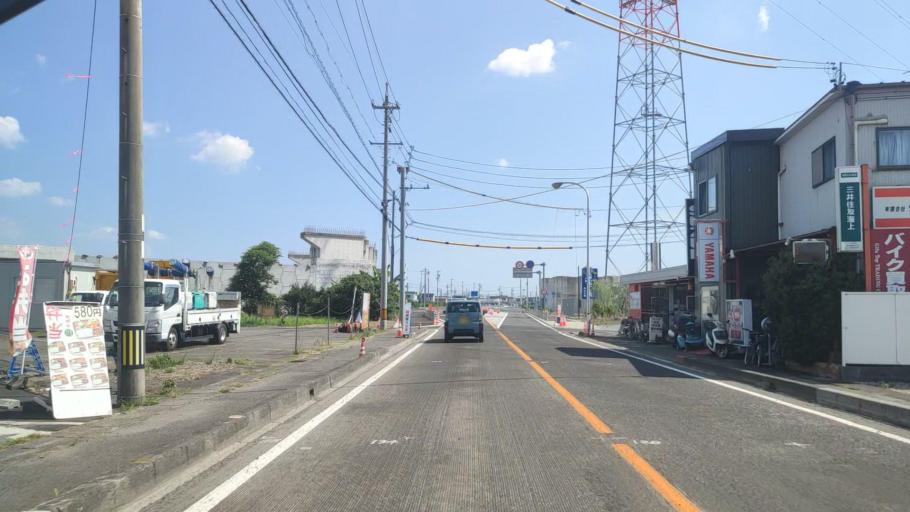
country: JP
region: Gifu
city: Godo
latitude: 35.4619
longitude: 136.6760
